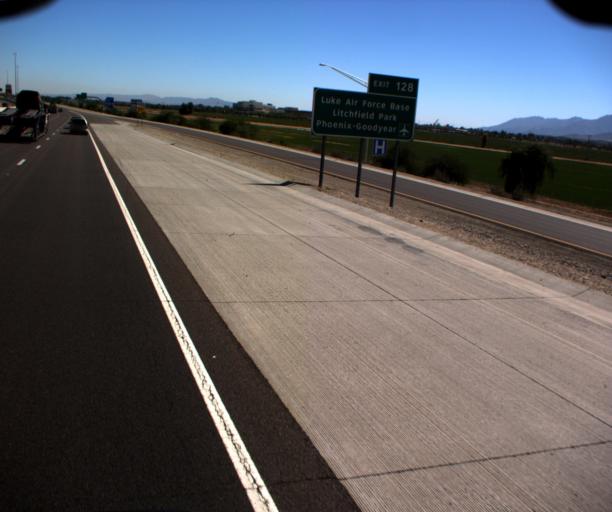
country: US
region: Arizona
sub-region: Maricopa County
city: Goodyear
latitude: 33.4593
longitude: -112.3728
